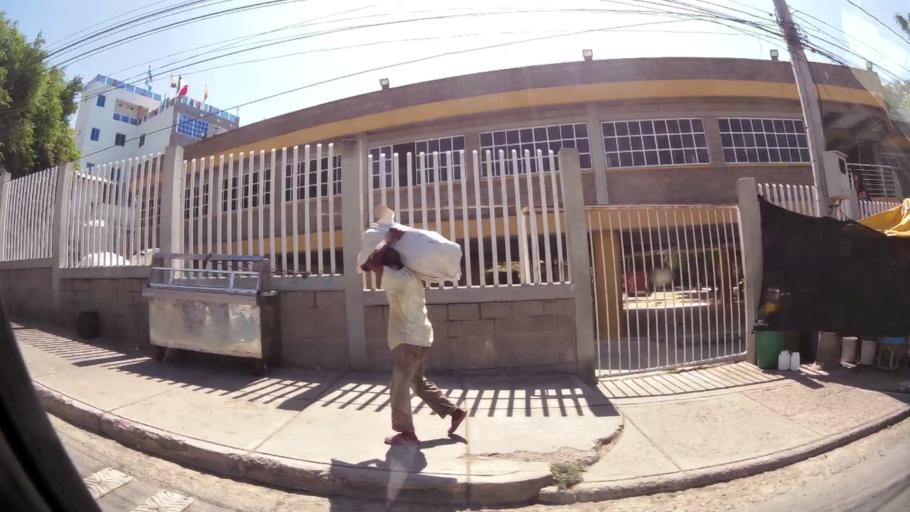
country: CO
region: Bolivar
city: Cartagena
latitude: 10.4354
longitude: -75.5272
